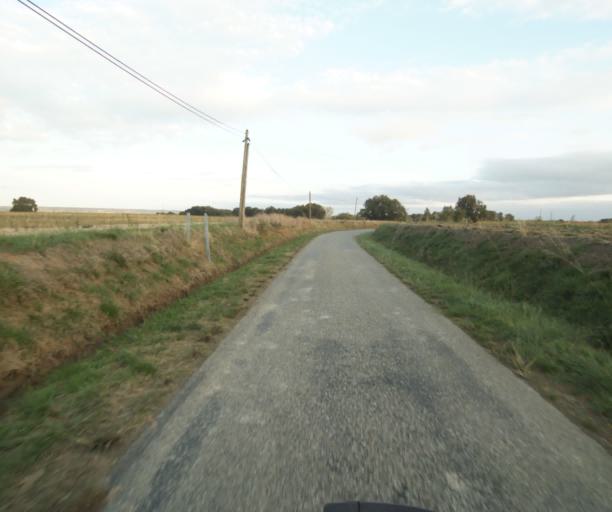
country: FR
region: Midi-Pyrenees
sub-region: Departement du Tarn-et-Garonne
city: Verdun-sur-Garonne
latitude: 43.8255
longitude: 1.2035
